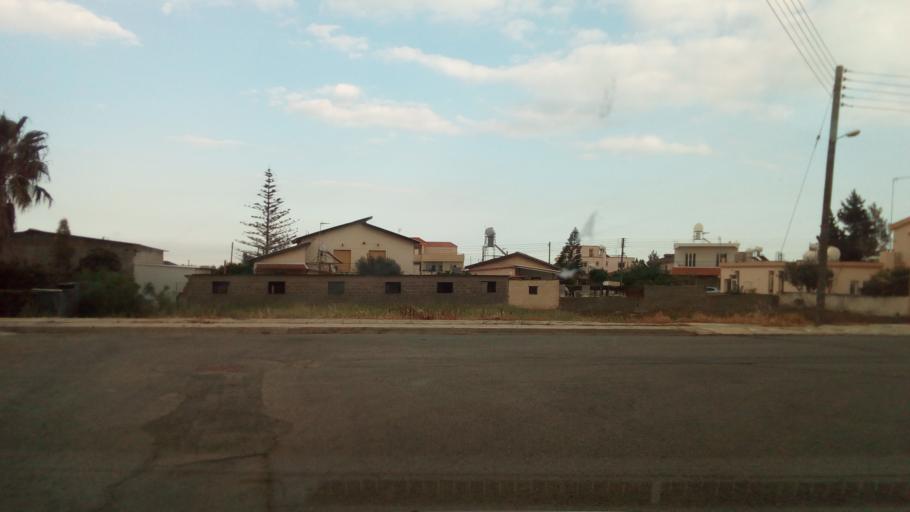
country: CY
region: Larnaka
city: Xylotymbou
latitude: 35.0207
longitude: 33.7453
